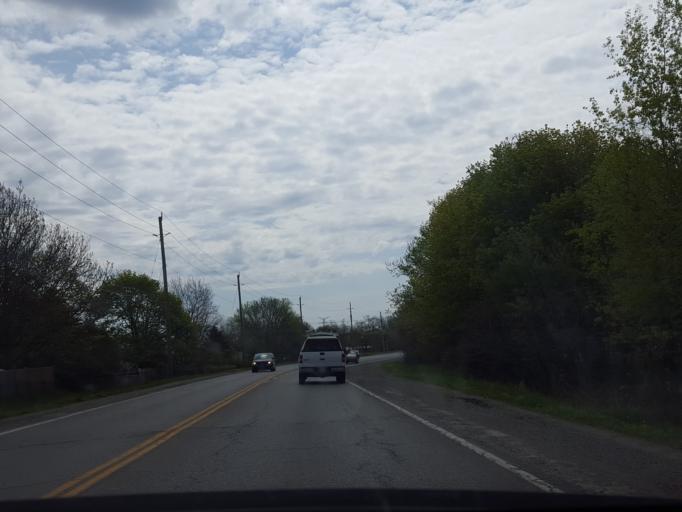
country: CA
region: Ontario
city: Oshawa
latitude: 43.9016
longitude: -78.6953
